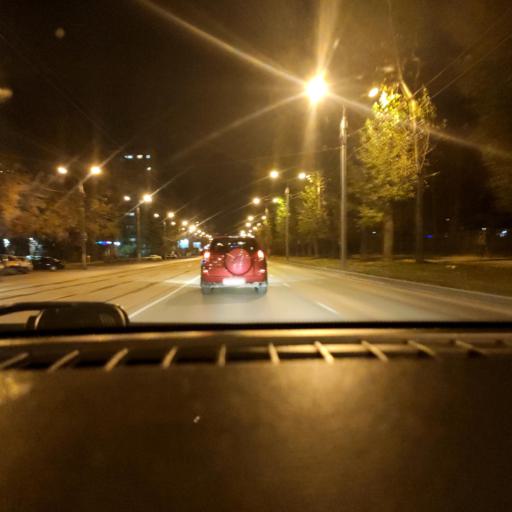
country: RU
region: Perm
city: Perm
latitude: 57.9834
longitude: 56.2039
